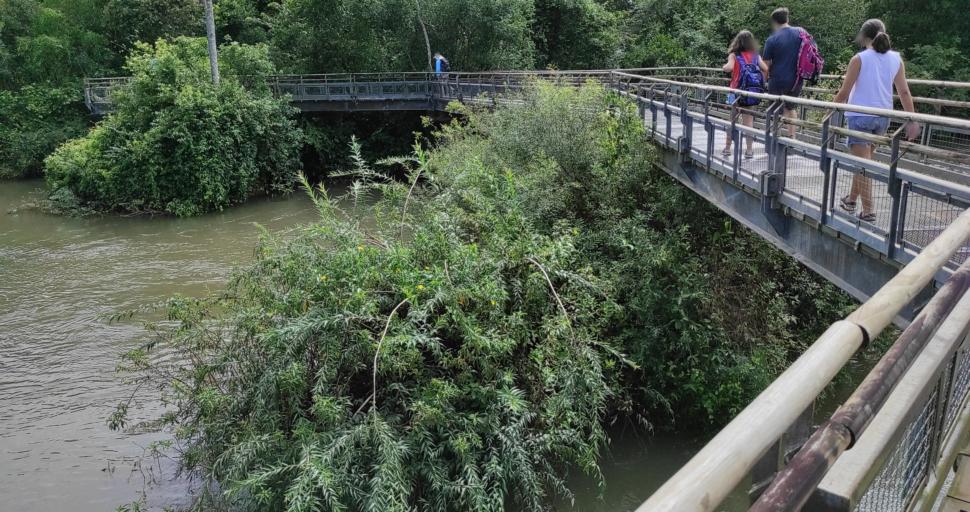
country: AR
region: Misiones
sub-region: Departamento de Iguazu
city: Puerto Iguazu
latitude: -25.7003
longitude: -54.4432
